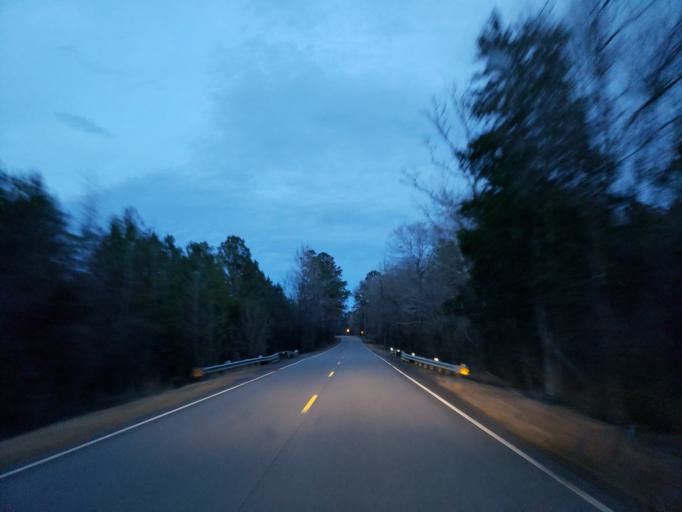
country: US
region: Alabama
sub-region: Greene County
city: Eutaw
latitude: 32.8899
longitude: -88.0417
